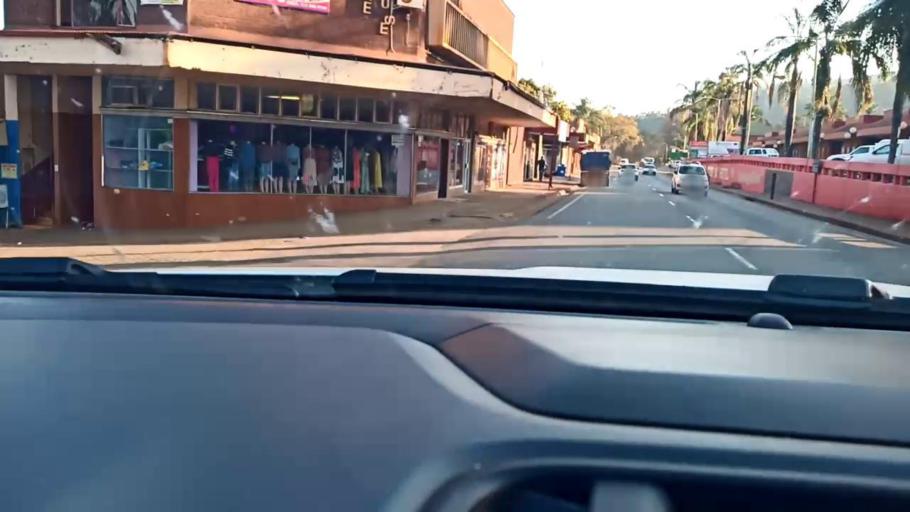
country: ZA
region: Limpopo
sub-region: Mopani District Municipality
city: Duiwelskloof
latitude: -23.6968
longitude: 30.1396
